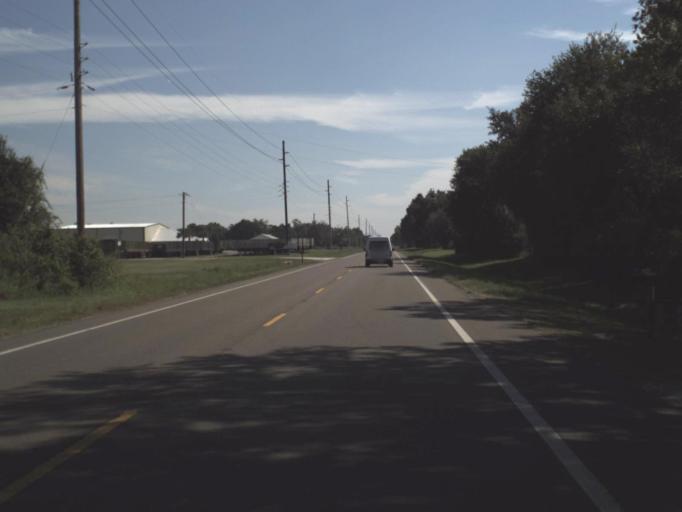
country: US
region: Florida
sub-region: Hardee County
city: Wauchula
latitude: 27.5514
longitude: -81.7655
